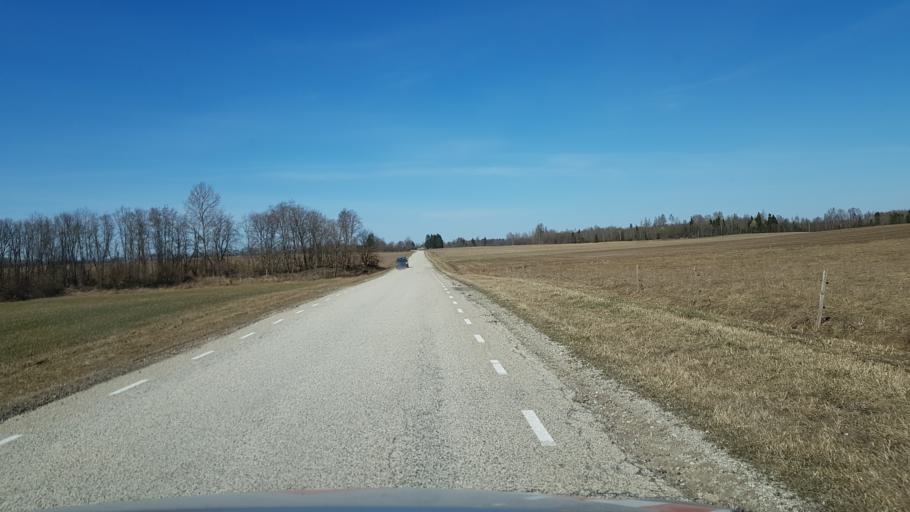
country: EE
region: Laeaene-Virumaa
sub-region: Vinni vald
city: Vinni
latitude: 59.0790
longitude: 26.5487
